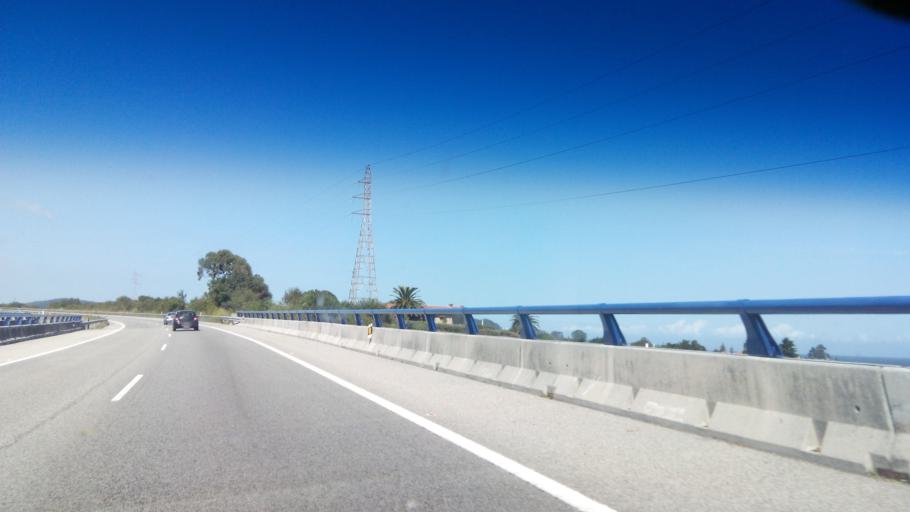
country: ES
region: Asturias
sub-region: Province of Asturias
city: Colunga
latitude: 43.4719
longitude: -5.2188
